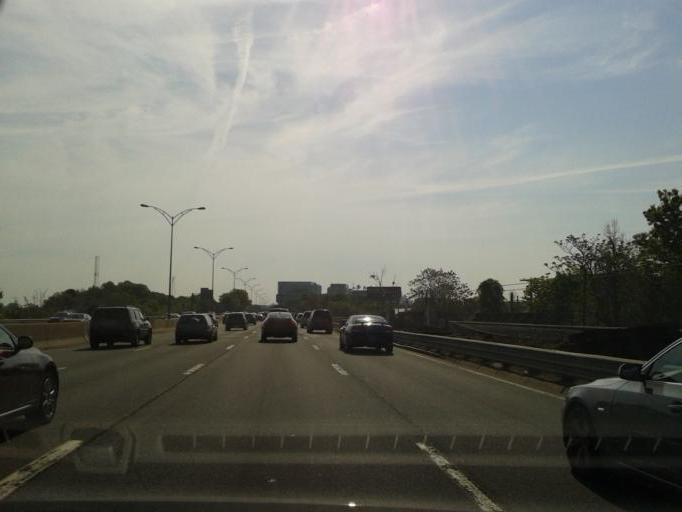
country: US
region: Massachusetts
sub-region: Middlesex County
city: Watertown
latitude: 42.3576
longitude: -71.1584
